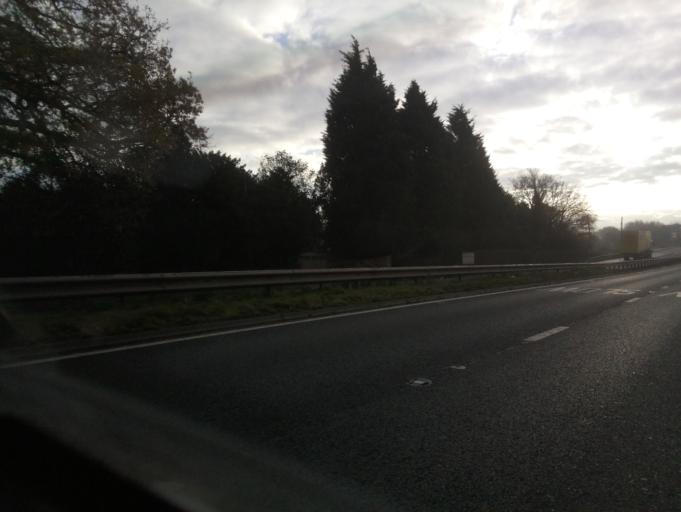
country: GB
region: England
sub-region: Staffordshire
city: Shenstone
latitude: 52.6474
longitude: -1.8073
